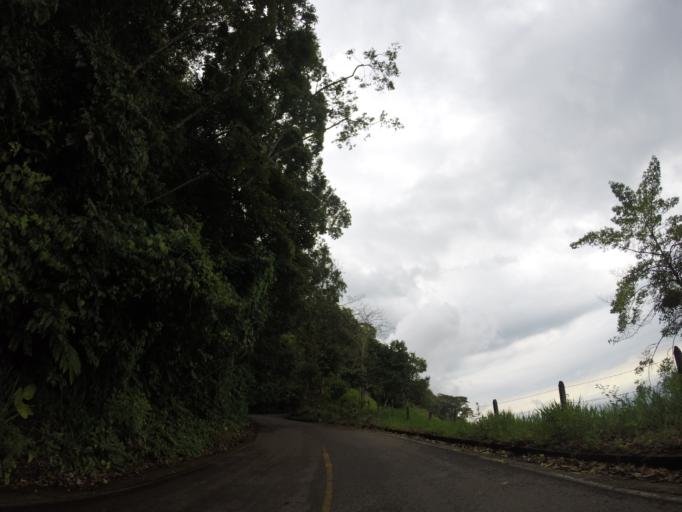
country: CO
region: Caldas
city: Victoria
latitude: 5.3206
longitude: -74.9298
